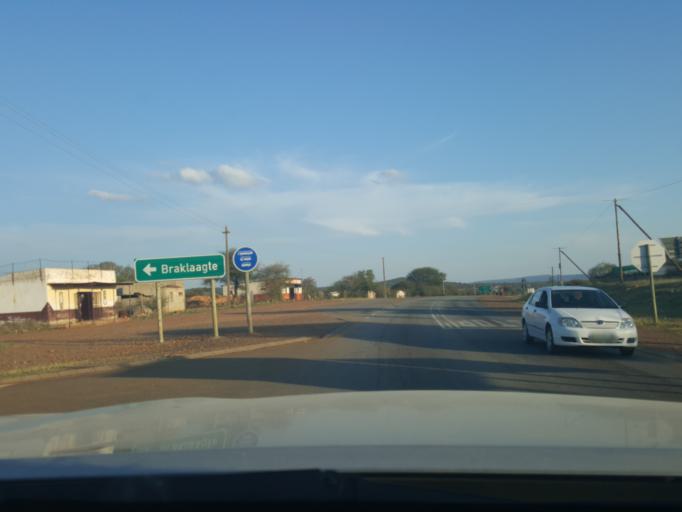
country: ZA
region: North-West
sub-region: Ngaka Modiri Molema District Municipality
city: Zeerust
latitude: -25.3861
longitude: 26.0843
